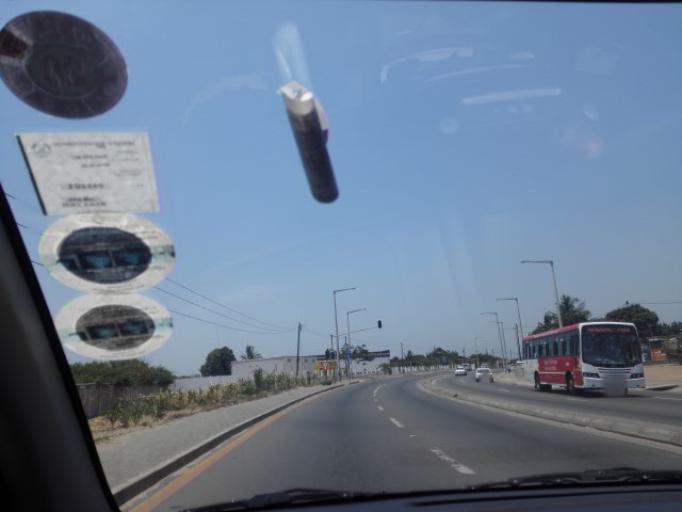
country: MZ
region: Maputo City
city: Maputo
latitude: -25.9172
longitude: 32.5661
